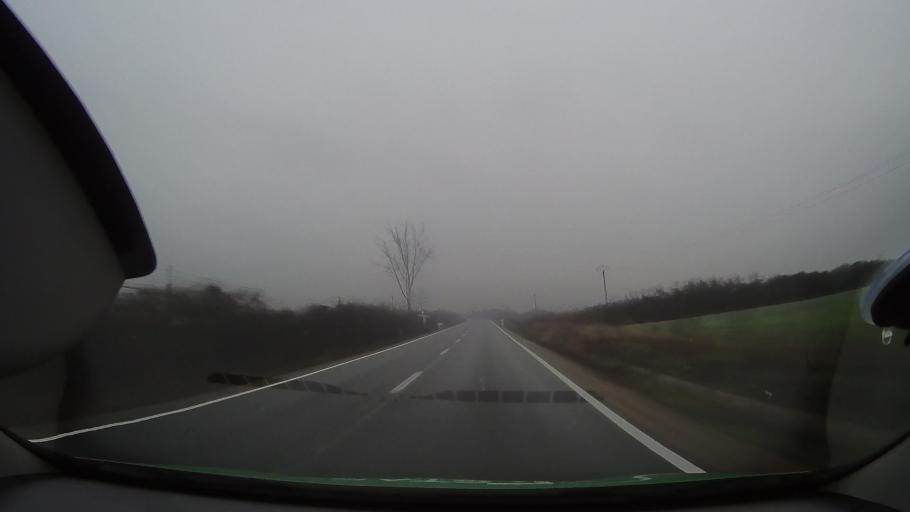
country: RO
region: Bihor
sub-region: Comuna Tinca
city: Tinca
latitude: 46.7299
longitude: 21.9430
